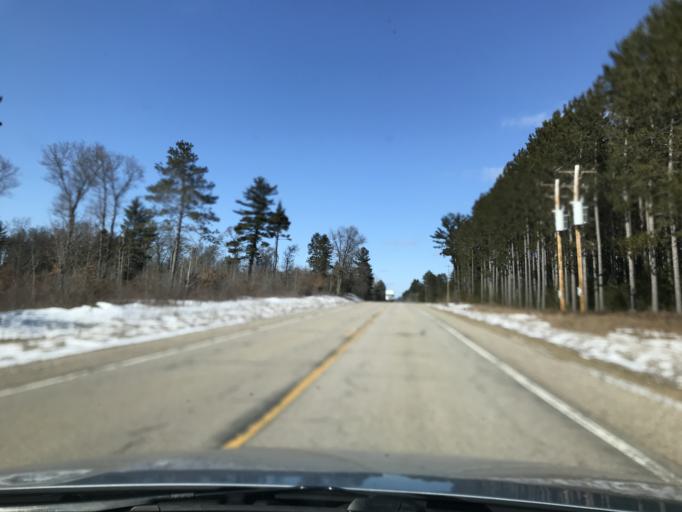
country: US
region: Wisconsin
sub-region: Marinette County
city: Niagara
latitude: 45.3829
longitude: -88.0998
